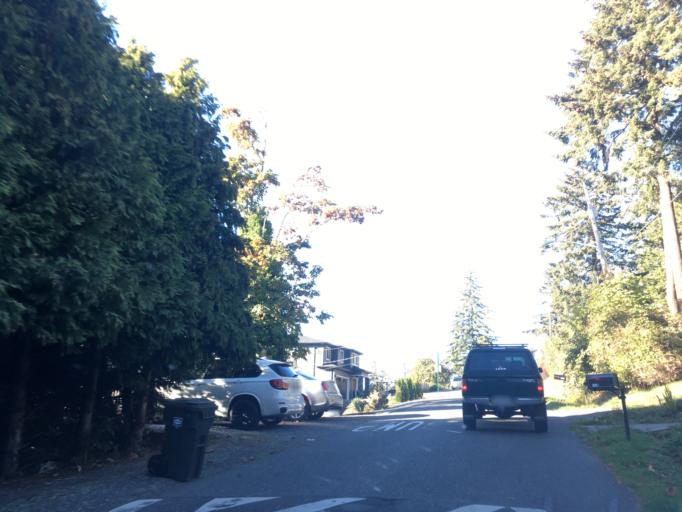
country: US
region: Washington
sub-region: Whatcom County
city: Bellingham
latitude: 48.7142
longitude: -122.4700
